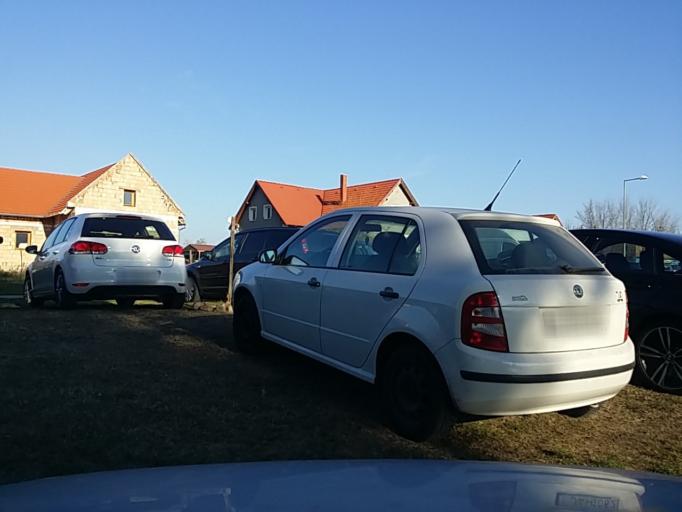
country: HU
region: Veszprem
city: Badacsonytomaj
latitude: 46.8530
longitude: 17.5182
